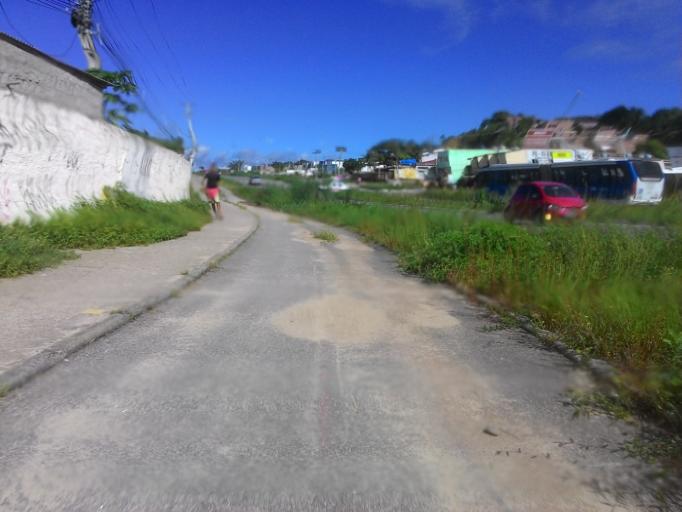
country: BR
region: Pernambuco
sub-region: Olinda
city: Olinda
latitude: -7.9761
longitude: -34.8632
